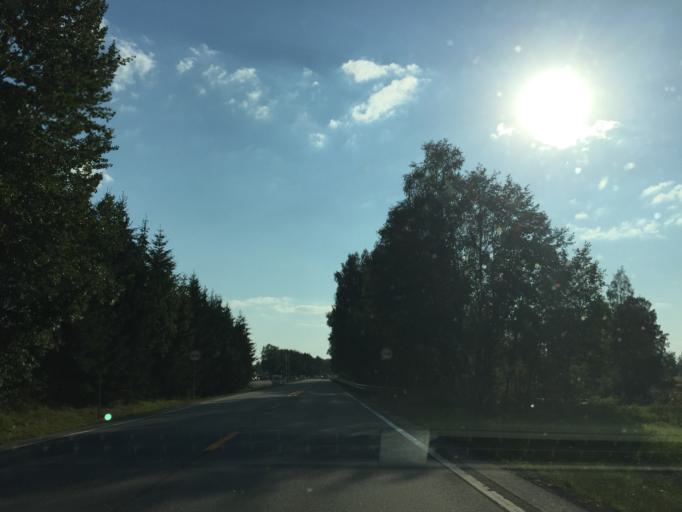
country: NO
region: Hedmark
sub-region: Sor-Odal
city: Skarnes
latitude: 60.2004
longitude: 11.5833
